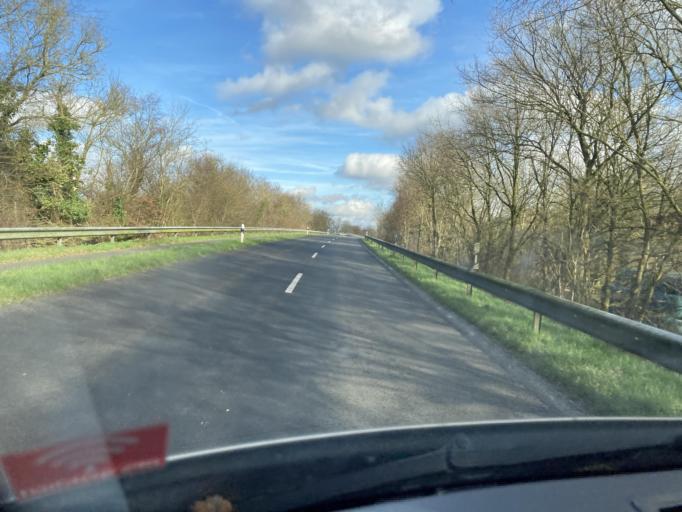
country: DE
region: Lower Saxony
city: Detern
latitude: 53.2452
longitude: 7.6683
